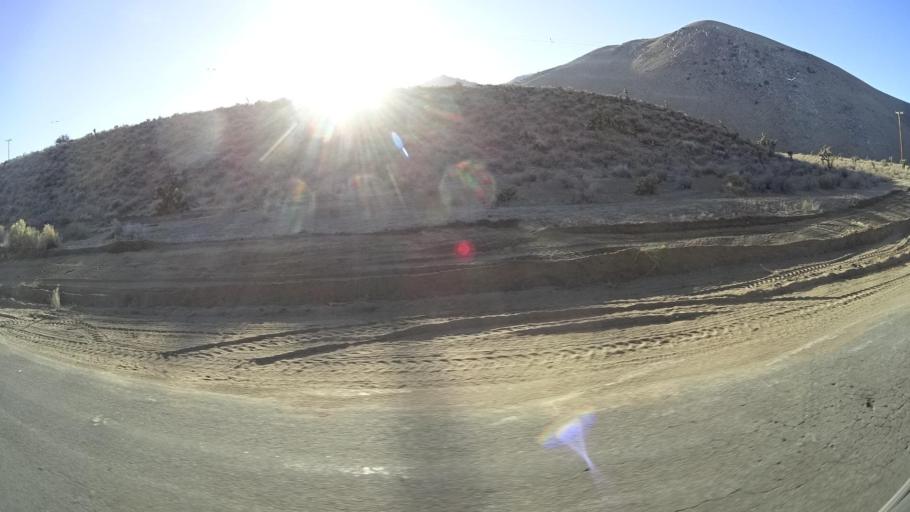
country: US
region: California
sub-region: Kern County
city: Weldon
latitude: 35.6056
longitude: -118.2432
